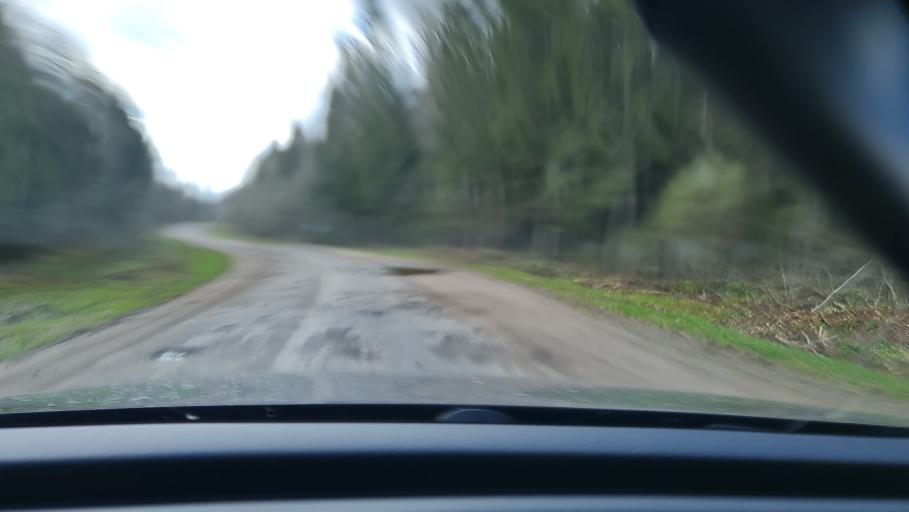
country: RU
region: Tverskaya
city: Toropets
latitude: 56.6261
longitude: 31.4327
